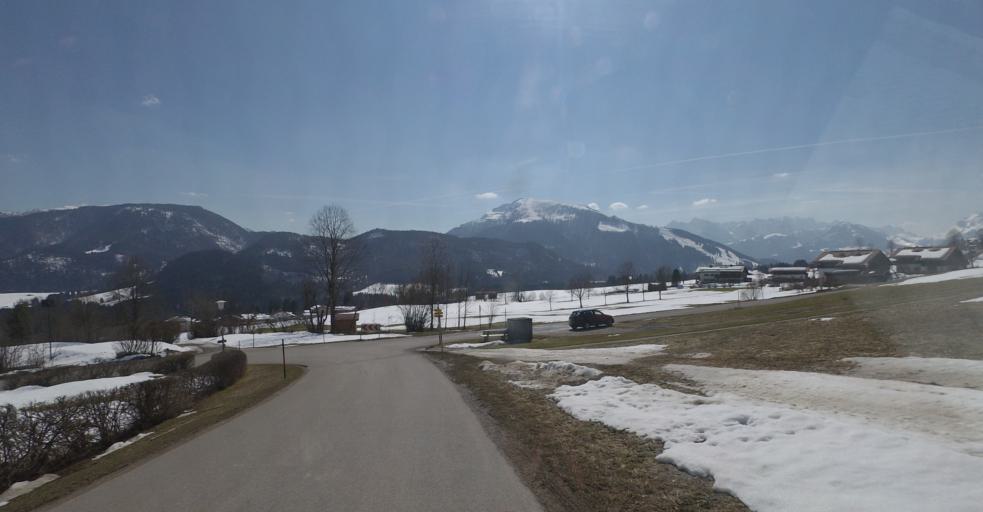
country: DE
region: Bavaria
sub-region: Upper Bavaria
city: Reit im Winkl
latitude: 47.6766
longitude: 12.4514
